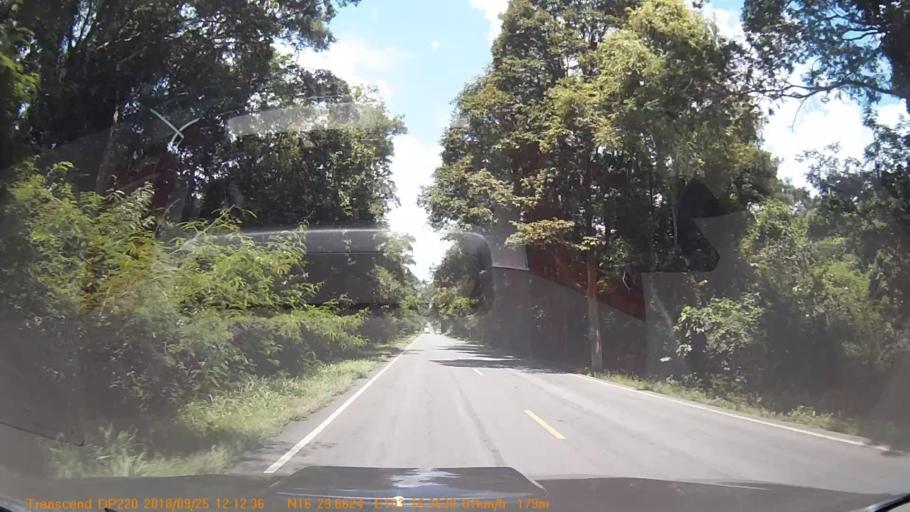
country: TH
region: Kalasin
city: Huai Mek
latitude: 16.4943
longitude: 103.2711
